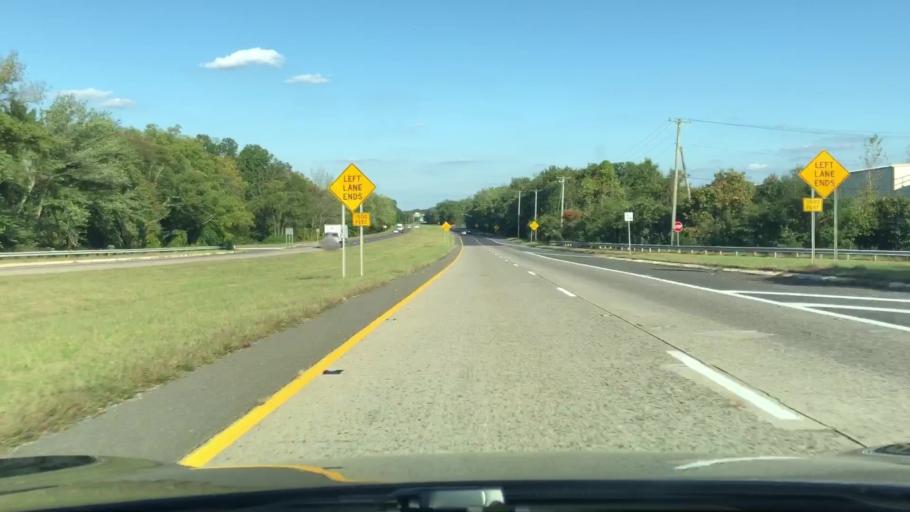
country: US
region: New Jersey
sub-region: Gloucester County
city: Gibbstown
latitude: 39.8030
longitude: -75.3224
